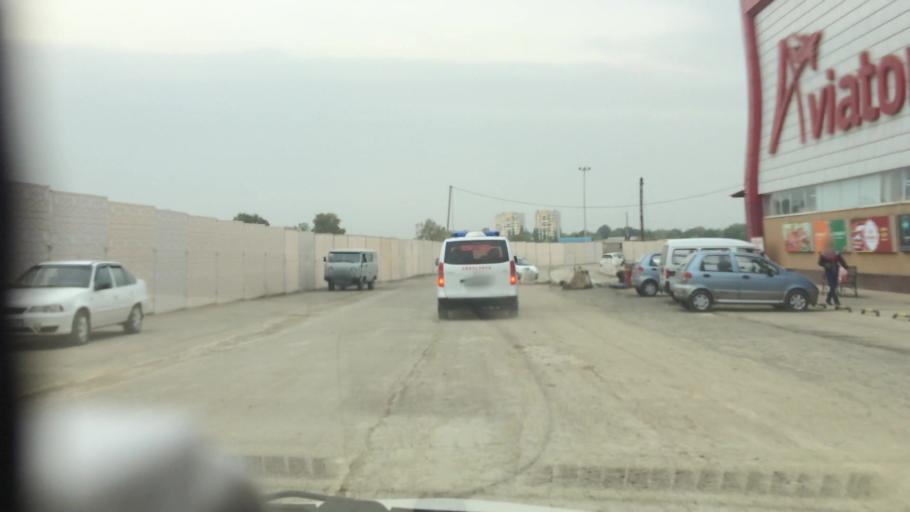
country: UZ
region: Toshkent
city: Salor
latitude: 41.3070
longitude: 69.3382
